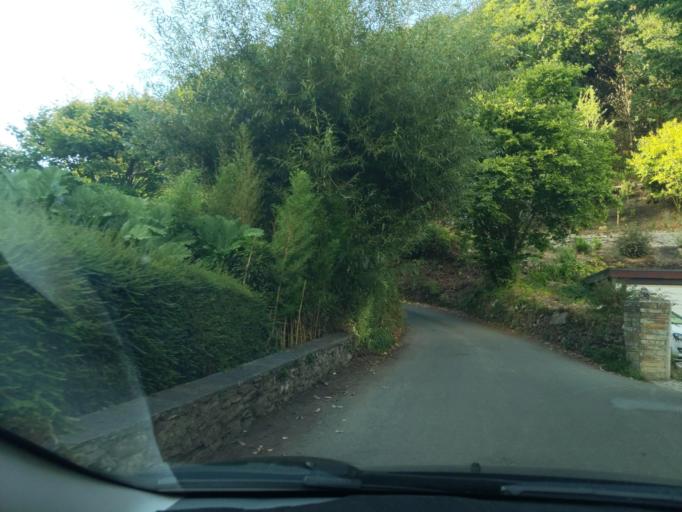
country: GB
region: England
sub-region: Devon
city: Salcombe
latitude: 50.2277
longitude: -3.7921
